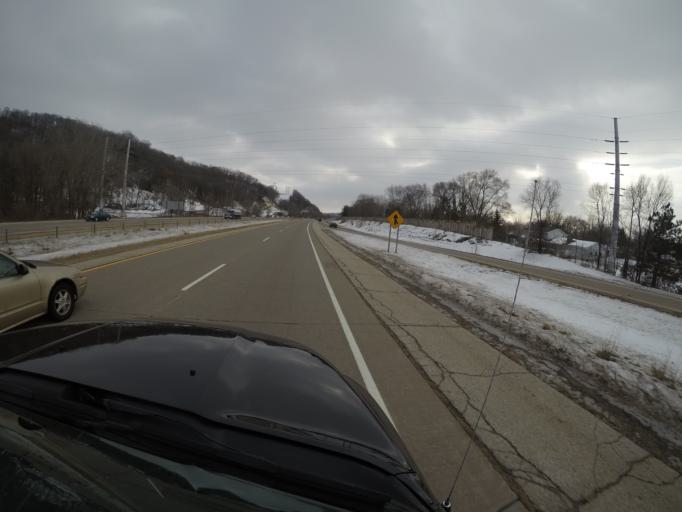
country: US
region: Wisconsin
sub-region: La Crosse County
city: Onalaska
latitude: 43.8952
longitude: -91.2177
